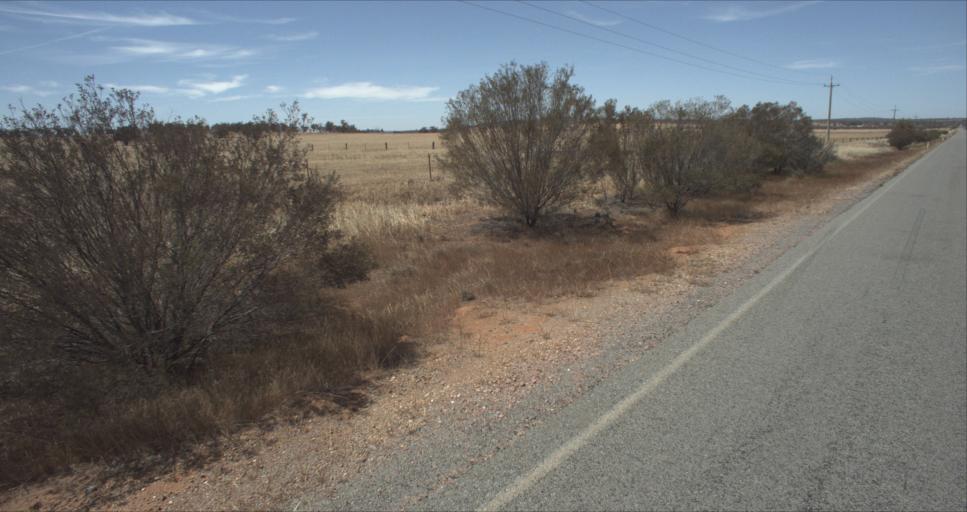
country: AU
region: New South Wales
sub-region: Leeton
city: Leeton
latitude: -34.6239
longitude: 146.4492
